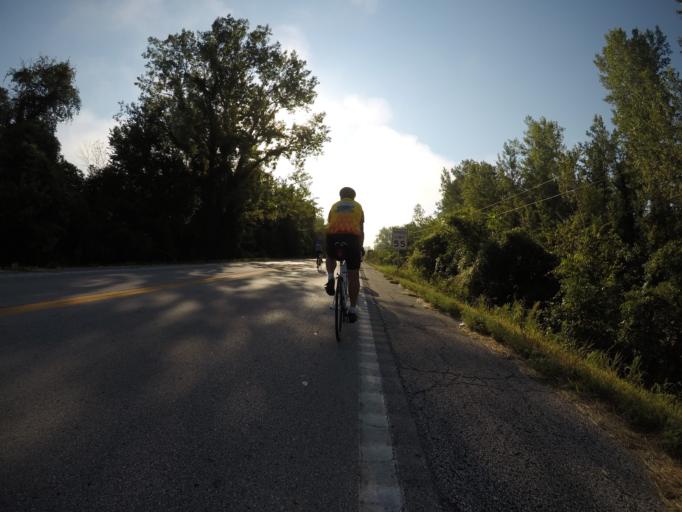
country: US
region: Kansas
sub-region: Leavenworth County
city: Leavenworth
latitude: 39.3309
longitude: -94.8935
